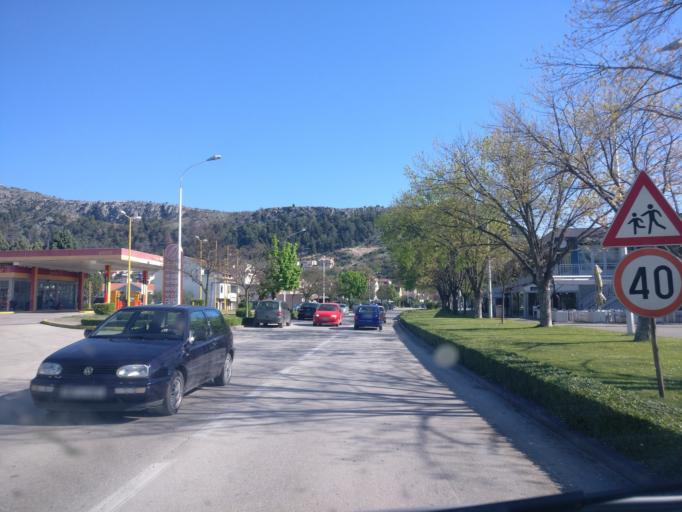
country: BA
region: Federation of Bosnia and Herzegovina
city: Capljina
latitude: 43.1120
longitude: 17.6998
